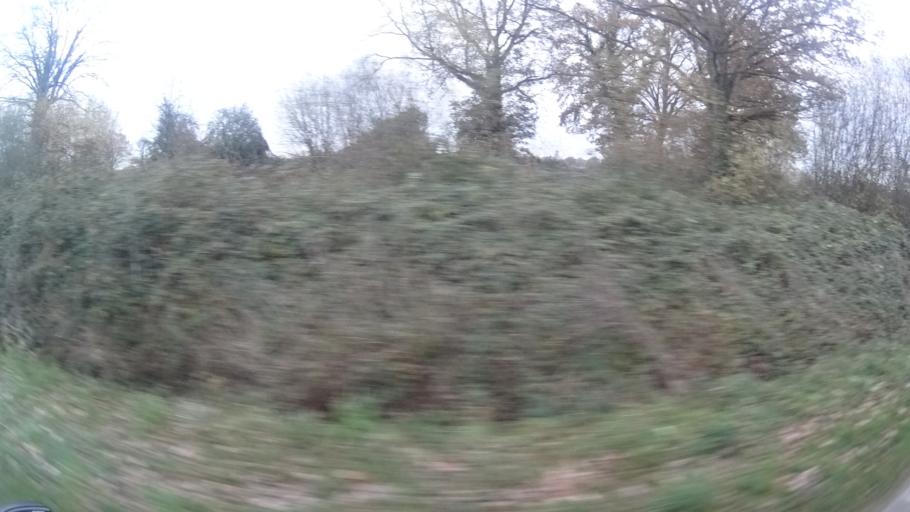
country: FR
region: Brittany
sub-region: Departement d'Ille-et-Vilaine
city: Langon
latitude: 47.6831
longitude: -1.8809
